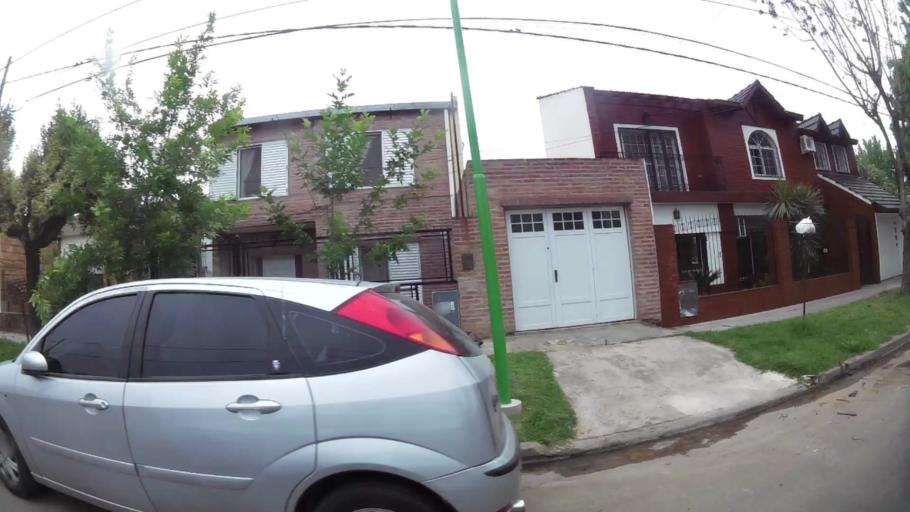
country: AR
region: Buenos Aires
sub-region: Partido de Campana
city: Campana
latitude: -34.1776
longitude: -58.9454
